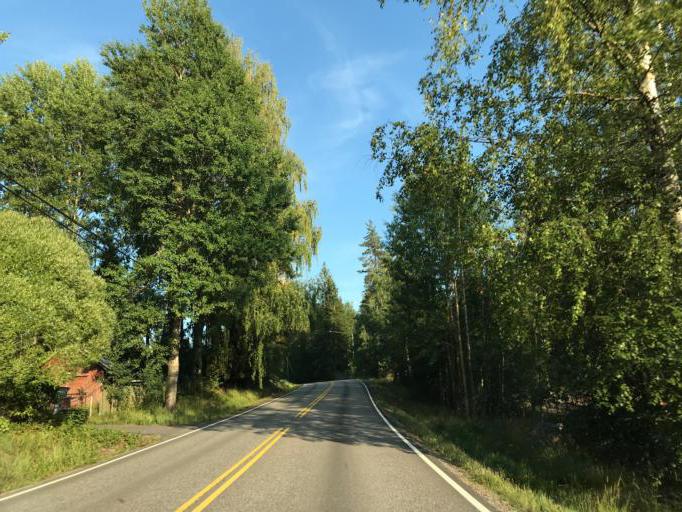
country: FI
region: Uusimaa
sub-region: Helsinki
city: Vihti
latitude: 60.4111
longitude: 24.4404
